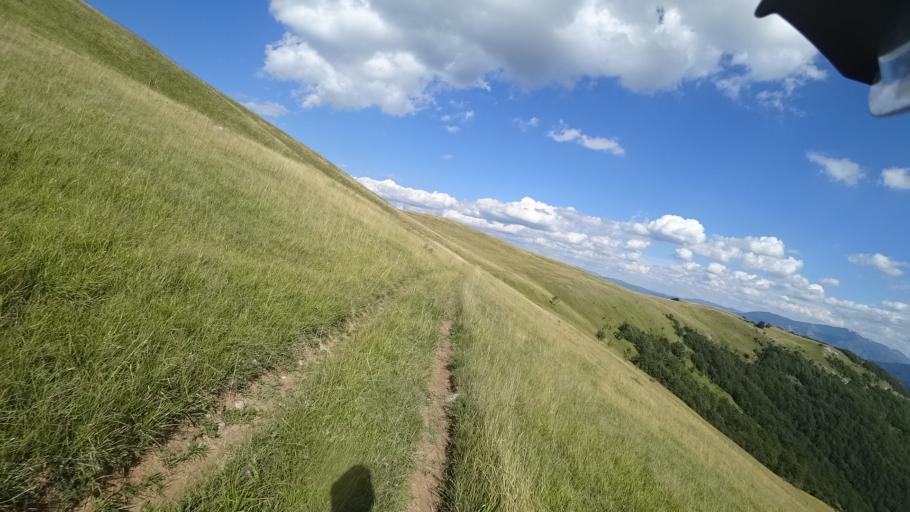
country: HR
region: Zadarska
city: Gracac
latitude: 44.3710
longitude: 16.0609
